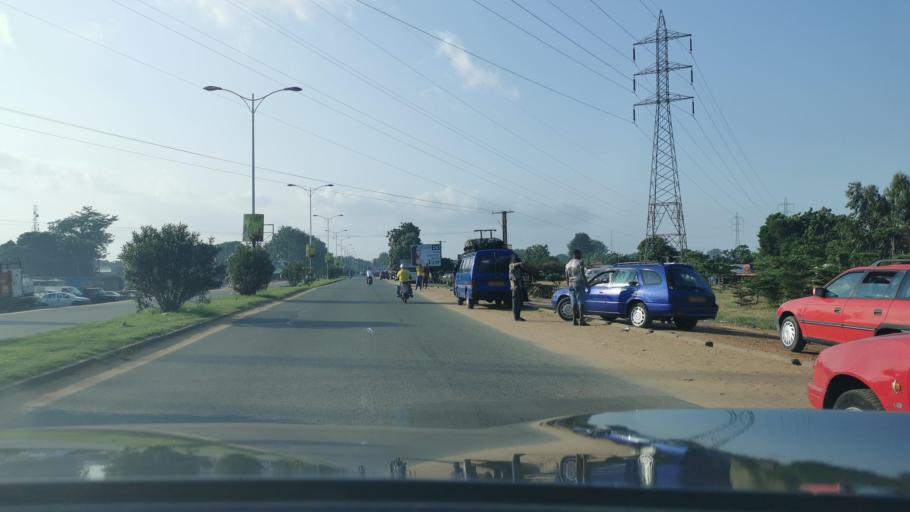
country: TG
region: Maritime
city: Lome
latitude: 6.1965
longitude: 1.2089
